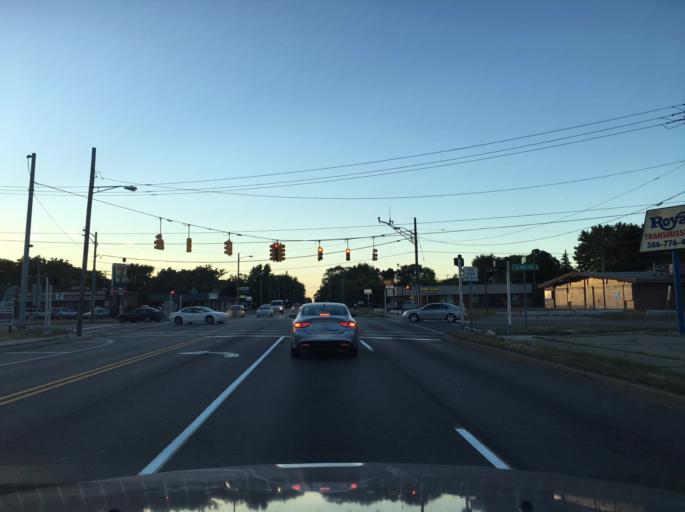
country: US
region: Michigan
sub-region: Macomb County
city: Roseville
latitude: 42.5092
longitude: -82.9358
